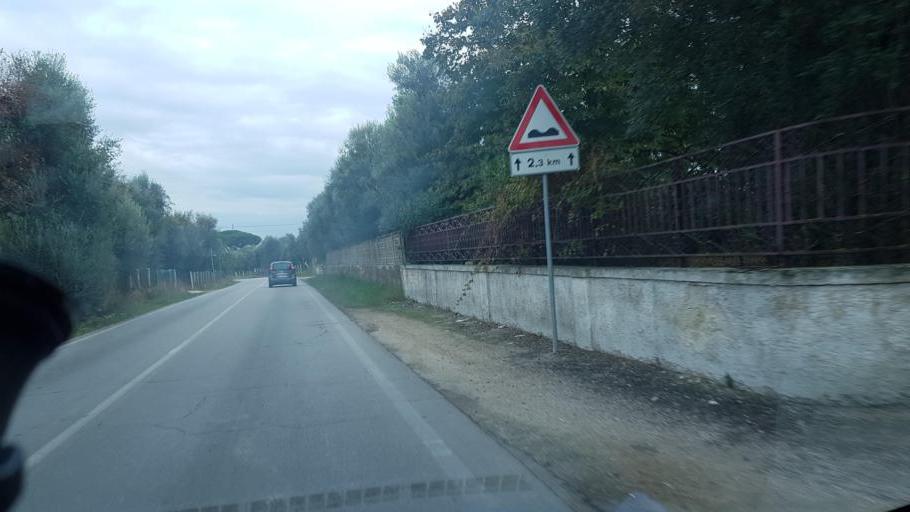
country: IT
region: Apulia
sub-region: Provincia di Brindisi
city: Francavilla Fontana
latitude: 40.5190
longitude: 17.6057
